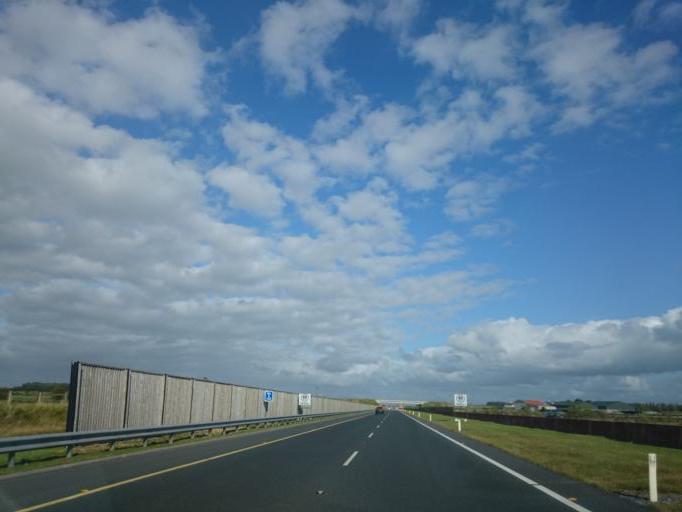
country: IE
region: Connaught
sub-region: County Galway
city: Oranmore
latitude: 53.2998
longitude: -8.8506
